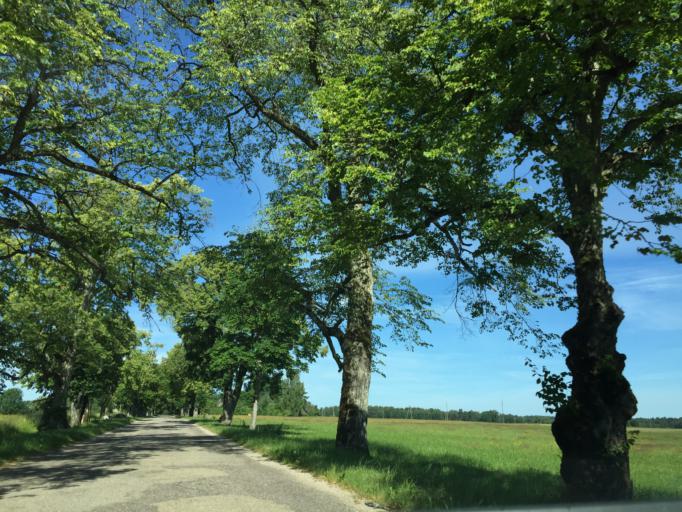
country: LV
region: Kuldigas Rajons
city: Kuldiga
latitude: 57.3254
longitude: 22.0253
